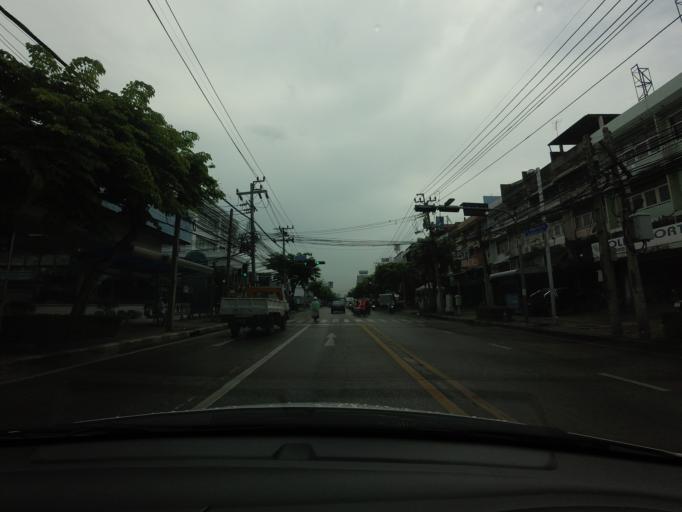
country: TH
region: Bangkok
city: Suan Luang
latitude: 13.7107
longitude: 100.6345
